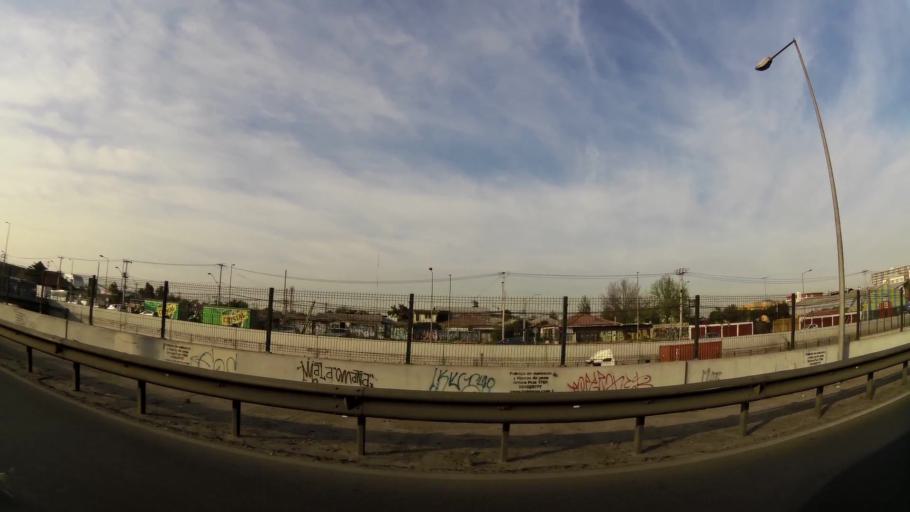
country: CL
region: Santiago Metropolitan
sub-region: Provincia de Santiago
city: La Pintana
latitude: -33.5365
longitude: -70.6661
